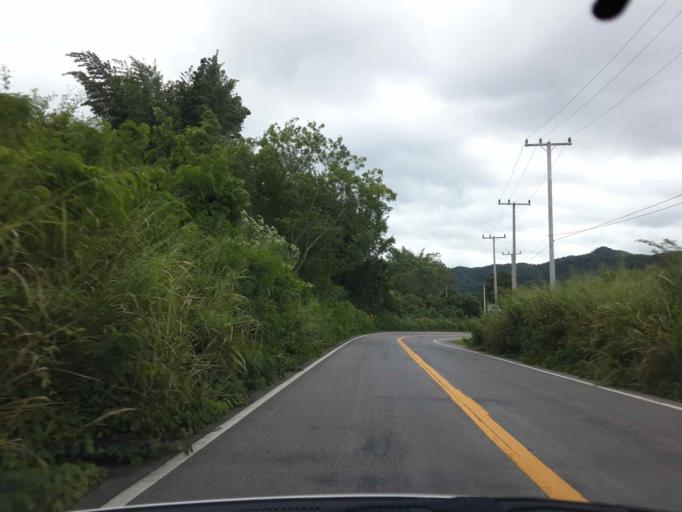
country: TH
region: Ratchaburi
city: Suan Phueng
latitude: 13.6642
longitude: 99.2073
